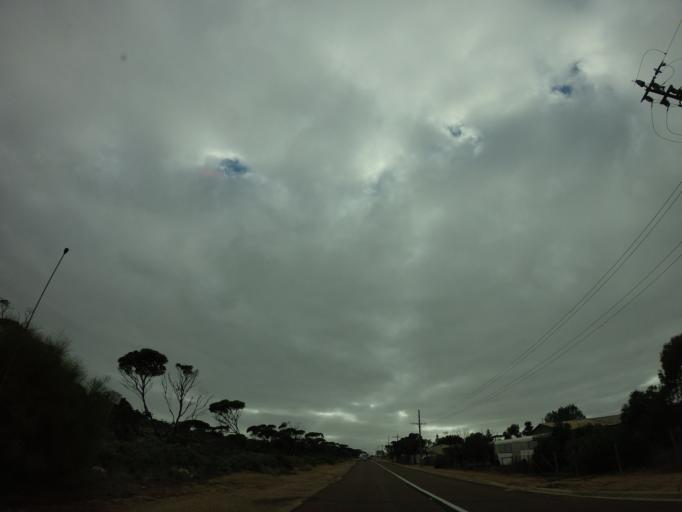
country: AU
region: South Australia
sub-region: Ceduna
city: Ceduna
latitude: -32.1219
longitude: 133.6804
